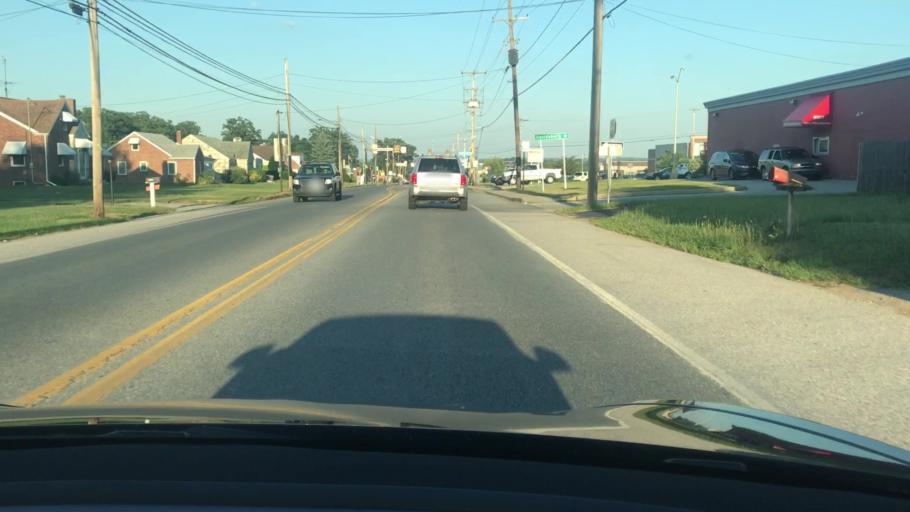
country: US
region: Pennsylvania
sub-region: York County
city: Weigelstown
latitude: 39.9843
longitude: -76.8257
